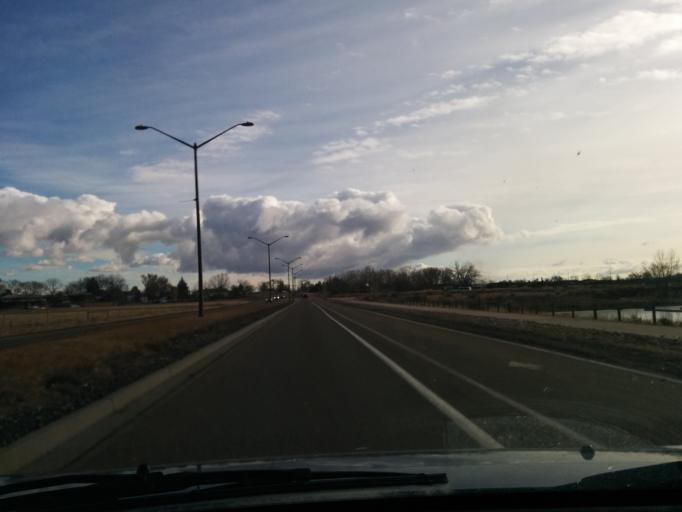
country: US
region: Colorado
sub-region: Larimer County
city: Fort Collins
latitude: 40.5668
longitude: -105.0189
